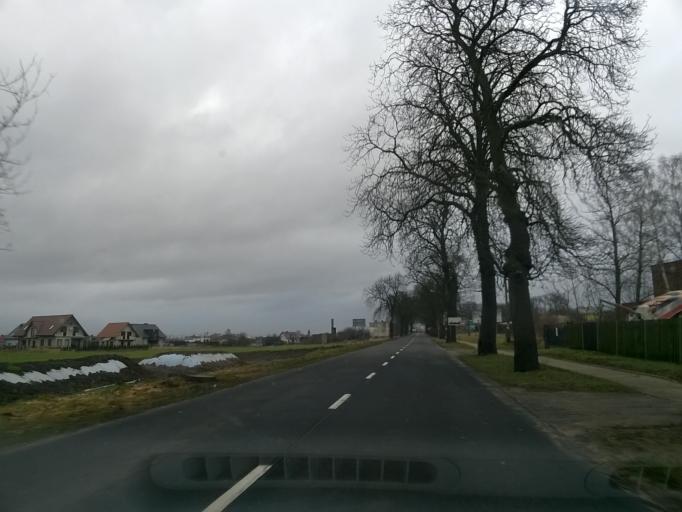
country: PL
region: Kujawsko-Pomorskie
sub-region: Powiat nakielski
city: Kcynia
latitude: 52.9885
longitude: 17.4752
